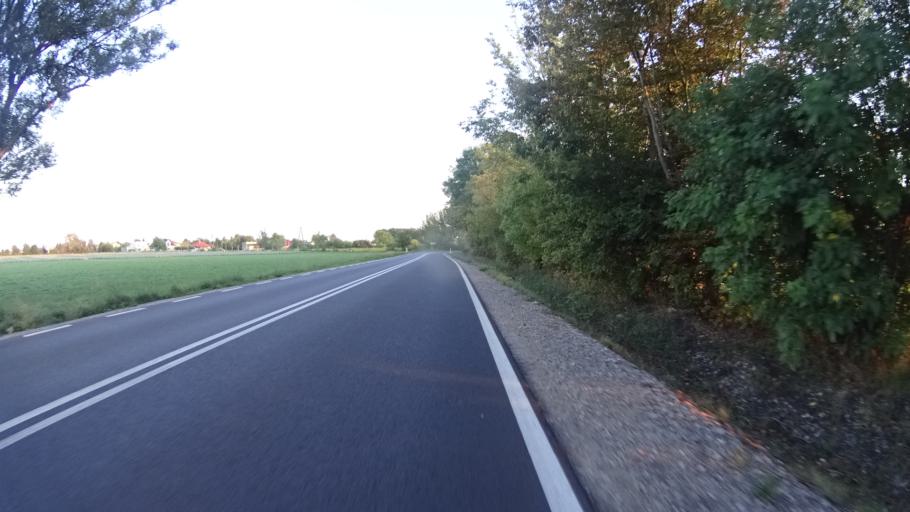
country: PL
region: Masovian Voivodeship
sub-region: Powiat warszawski zachodni
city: Ozarow Mazowiecki
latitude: 52.2243
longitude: 20.7736
